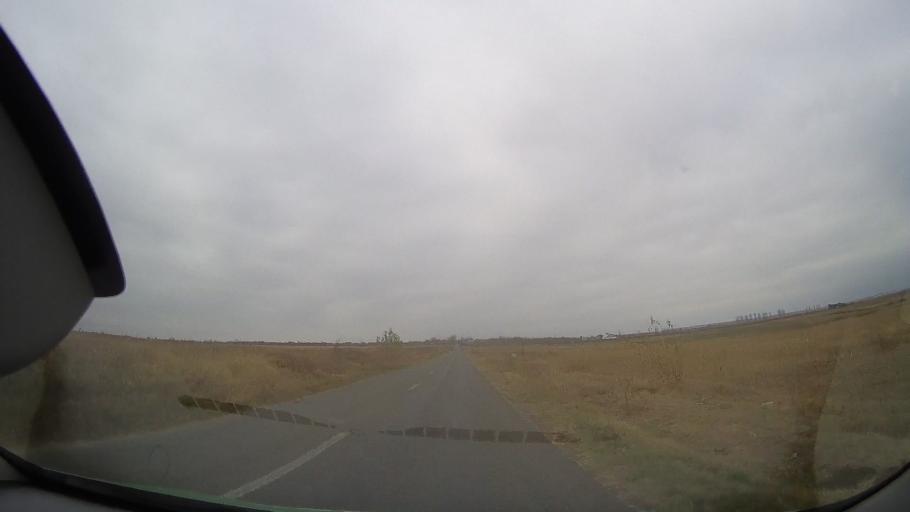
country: RO
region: Buzau
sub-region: Comuna Luciu
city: Luciu
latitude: 44.9784
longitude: 27.0509
